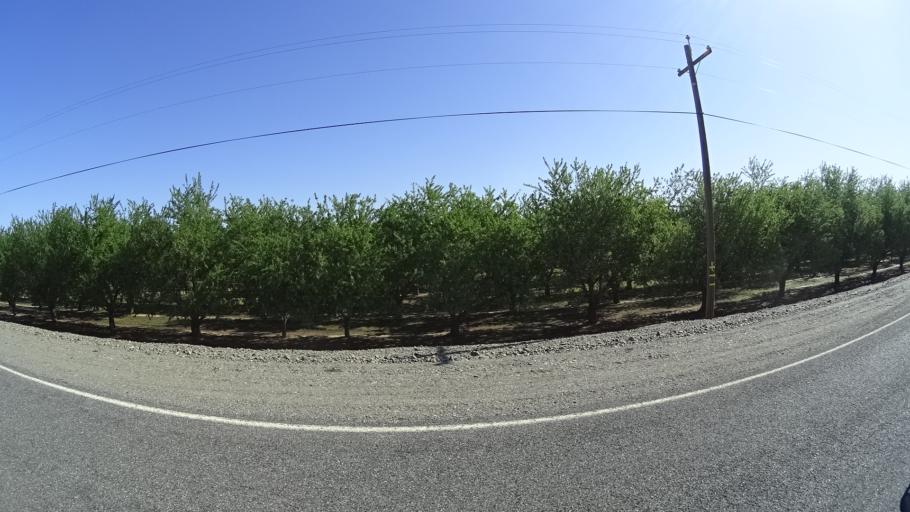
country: US
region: California
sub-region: Glenn County
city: Hamilton City
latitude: 39.7792
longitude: -122.0417
